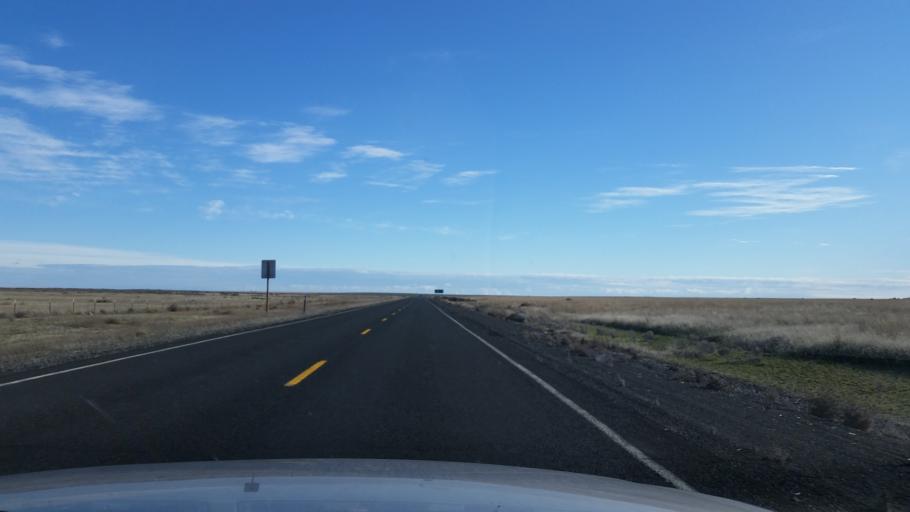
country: US
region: Washington
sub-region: Grant County
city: Moses Lake North
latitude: 47.3644
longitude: -118.9751
